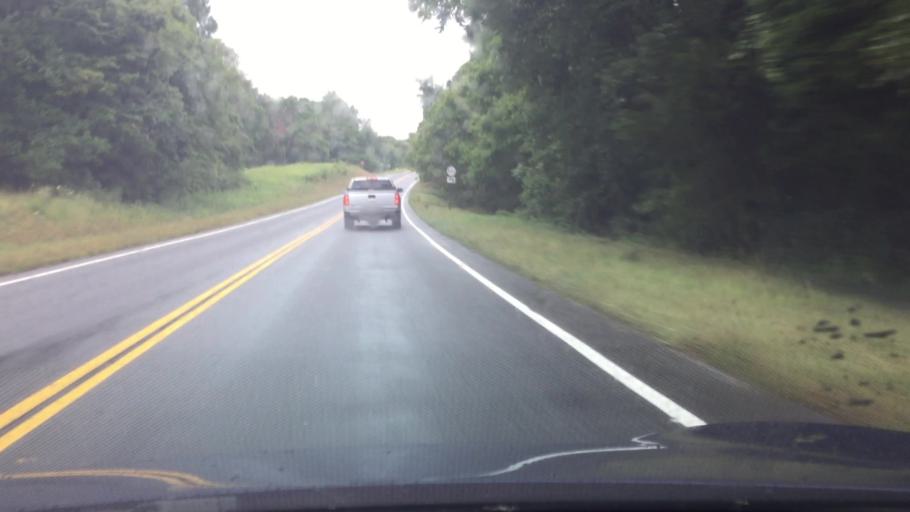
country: US
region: Virginia
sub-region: Bedford County
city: Forest
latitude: 37.3660
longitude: -79.3971
